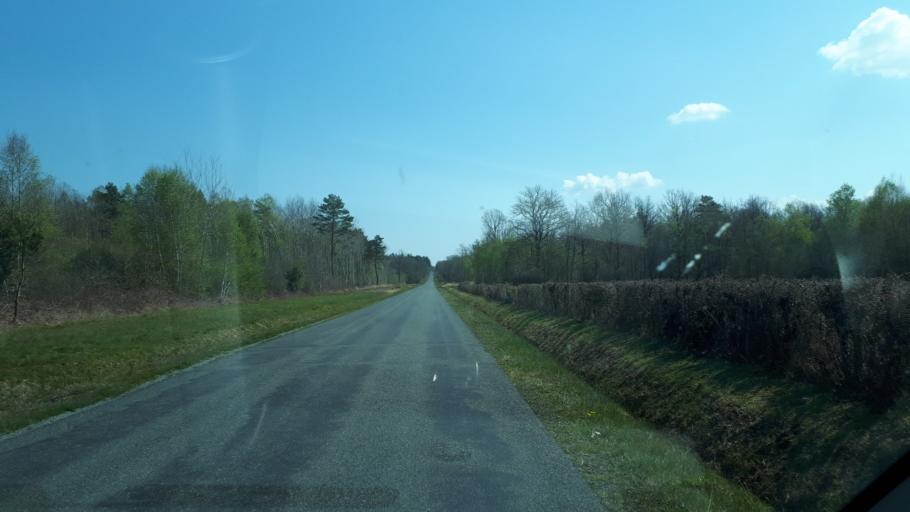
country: FR
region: Centre
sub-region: Departement du Cher
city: Neuvy-sur-Barangeon
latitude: 47.3188
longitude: 2.1620
